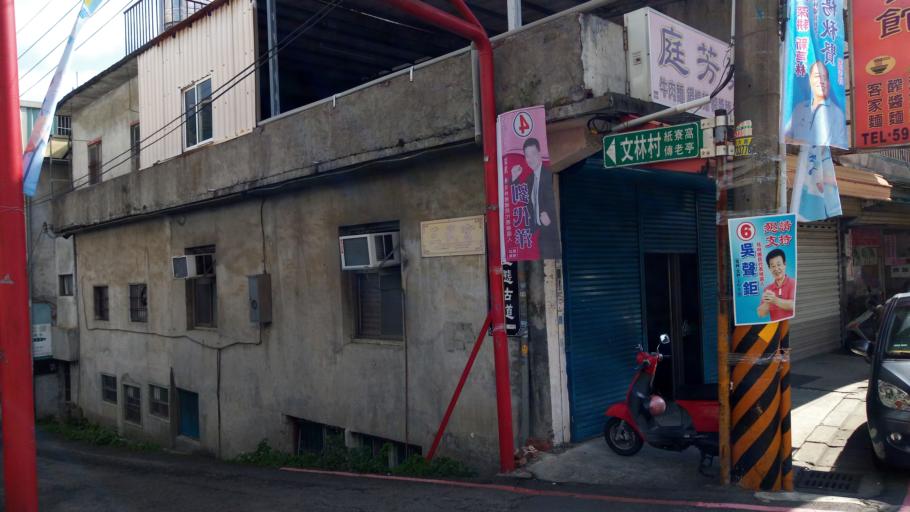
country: TW
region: Taiwan
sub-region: Hsinchu
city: Zhubei
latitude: 24.7748
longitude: 121.0816
